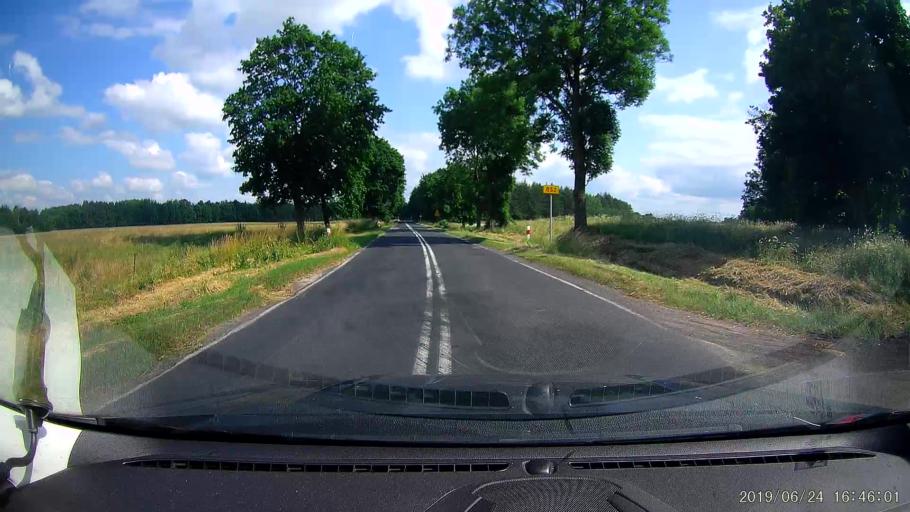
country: PL
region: Lublin Voivodeship
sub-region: Powiat tomaszowski
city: Laszczow
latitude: 50.5299
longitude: 23.6727
